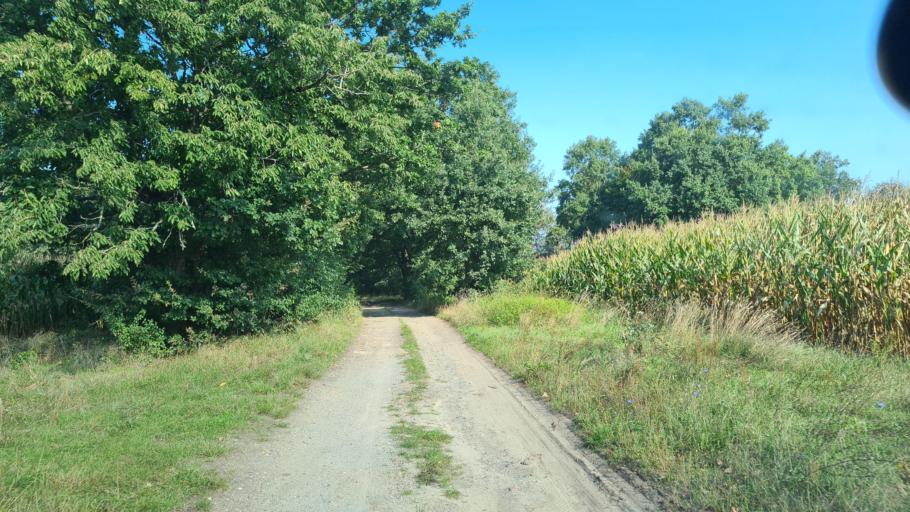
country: DE
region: Brandenburg
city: Luckau
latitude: 51.8431
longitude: 13.6874
